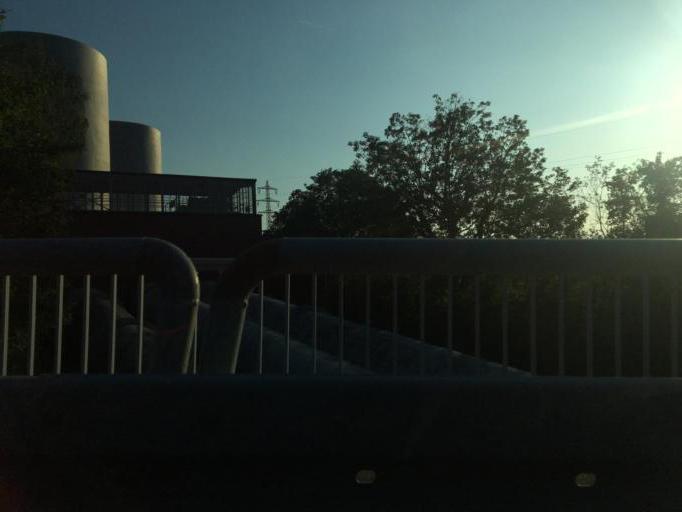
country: DE
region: Saxony
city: Coswig
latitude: 51.0857
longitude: 13.6045
